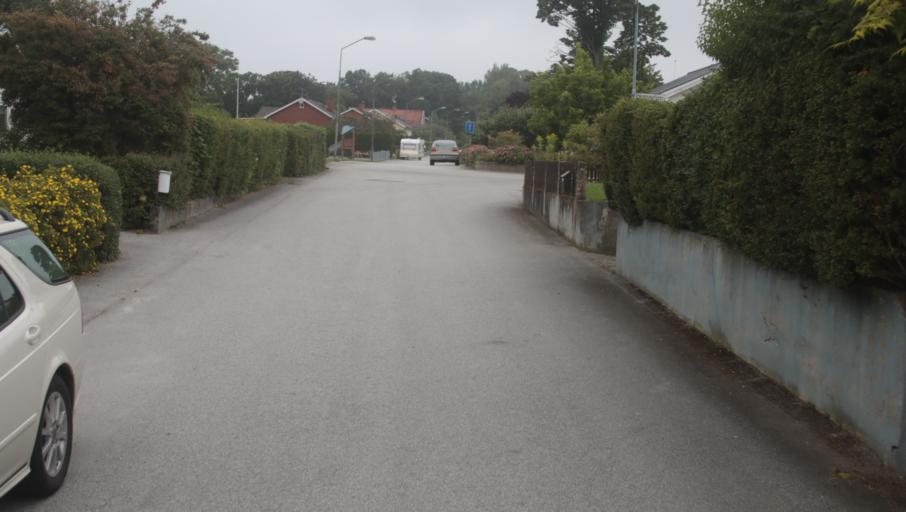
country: SE
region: Blekinge
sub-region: Karlshamns Kommun
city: Karlshamn
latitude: 56.2036
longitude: 14.9454
